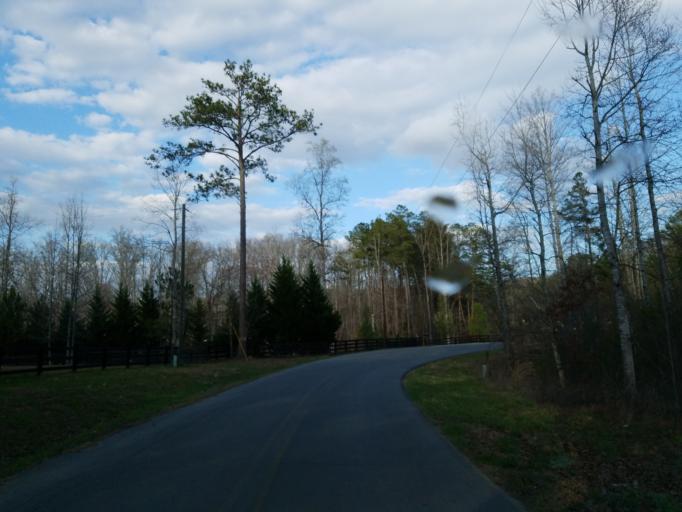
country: US
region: Georgia
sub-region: Bartow County
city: Rydal
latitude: 34.4804
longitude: -84.6619
